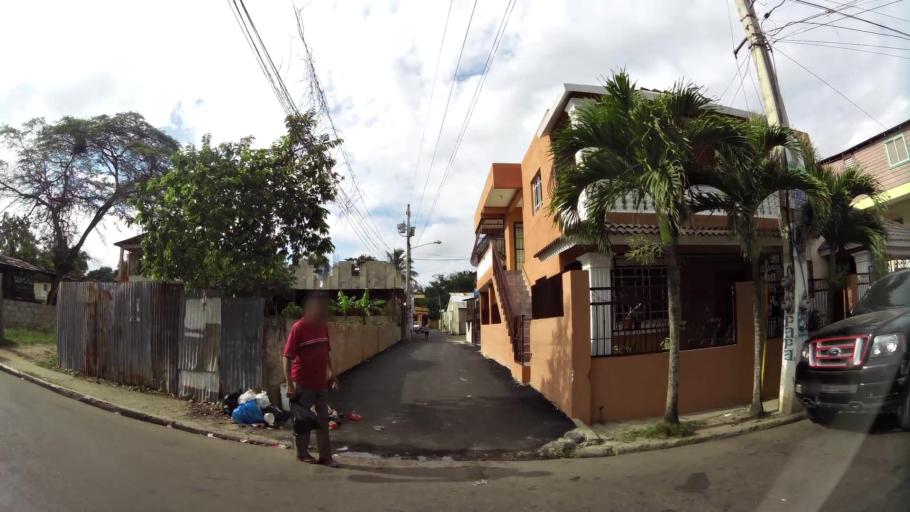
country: DO
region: Santiago
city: Santiago de los Caballeros
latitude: 19.4269
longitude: -70.6692
